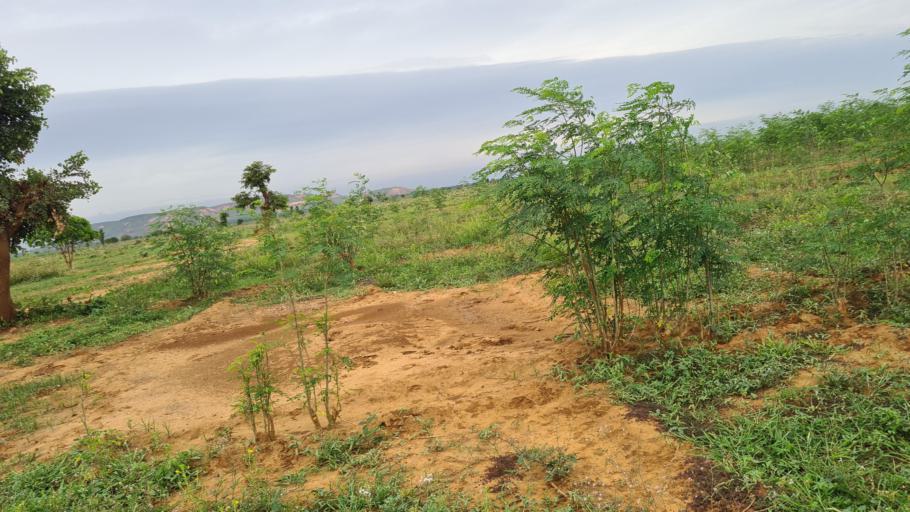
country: NE
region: Tahoua
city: Birni N Konni
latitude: 13.8366
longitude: 5.2681
